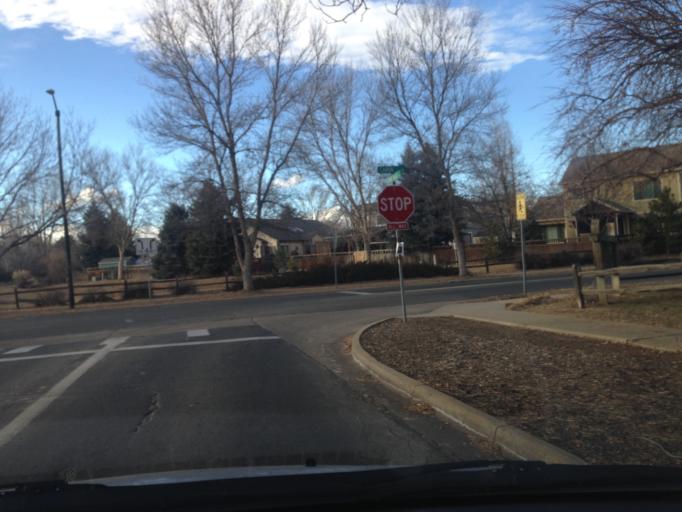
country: US
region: Colorado
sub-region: Boulder County
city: Lafayette
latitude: 39.9894
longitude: -105.1095
